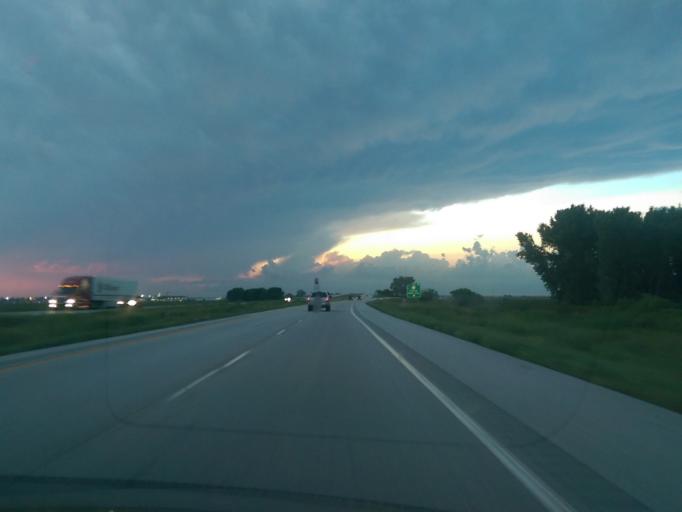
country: US
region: Nebraska
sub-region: Otoe County
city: Nebraska City
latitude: 40.6833
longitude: -95.7784
